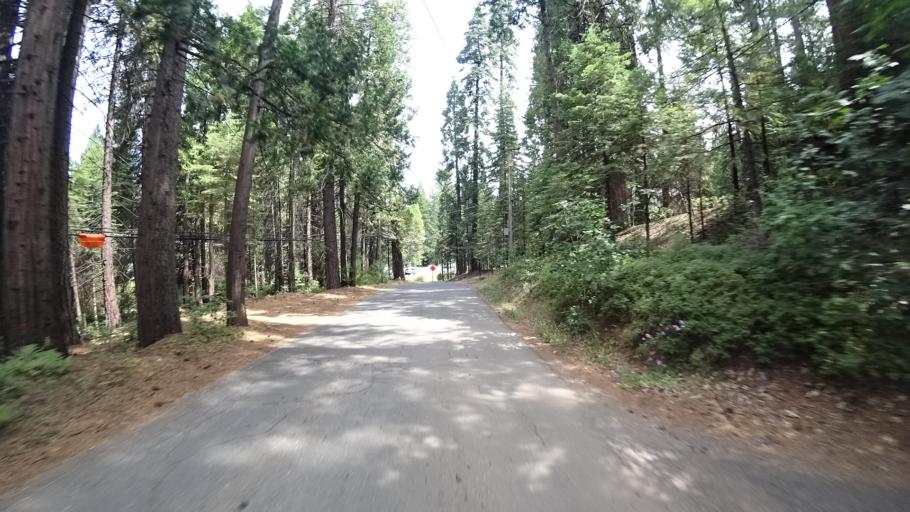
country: US
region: California
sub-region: Calaveras County
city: Arnold
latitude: 38.2503
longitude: -120.3578
